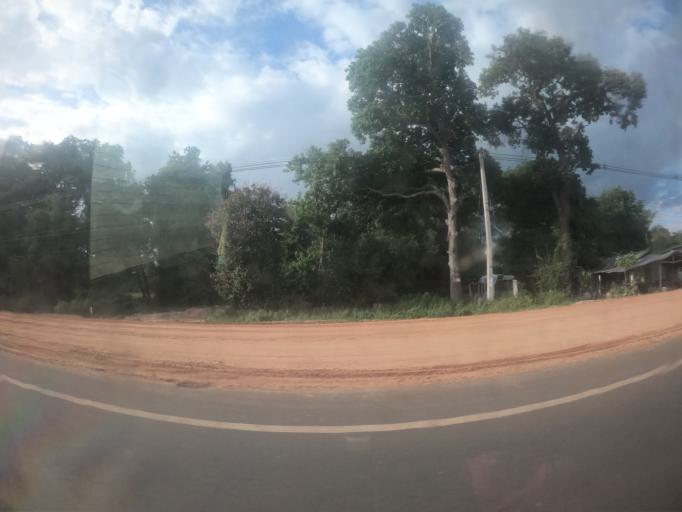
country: TH
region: Surin
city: Kap Choeng
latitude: 14.4734
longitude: 103.6050
